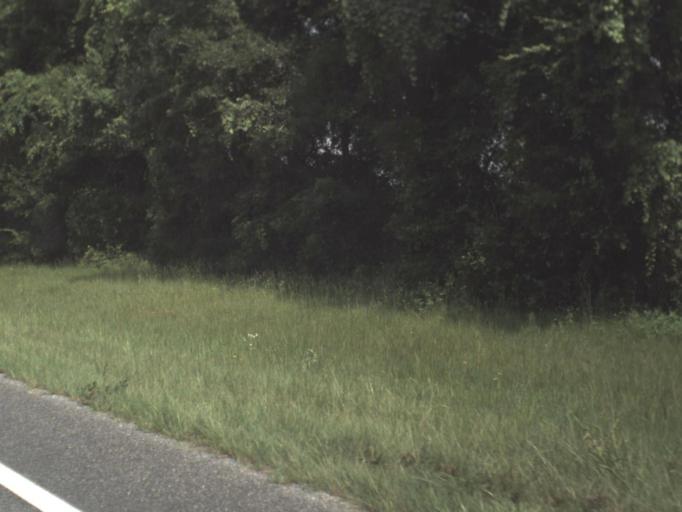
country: US
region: Florida
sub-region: Levy County
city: Chiefland
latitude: 29.4750
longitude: -82.8113
